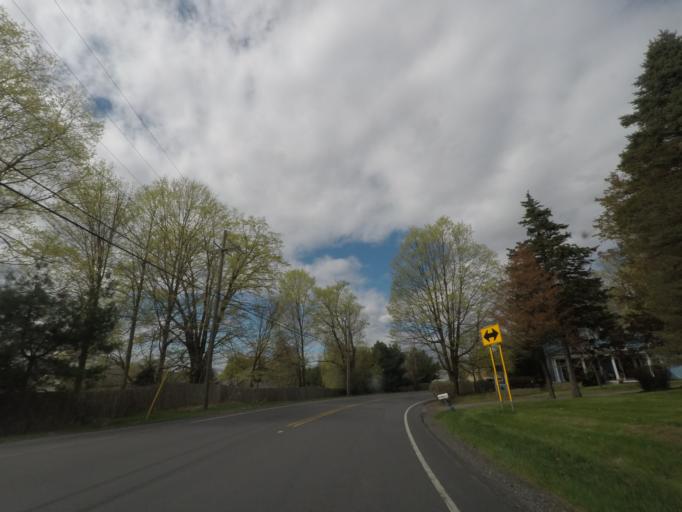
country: US
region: New York
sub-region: Columbia County
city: Valatie
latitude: 42.4063
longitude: -73.6752
